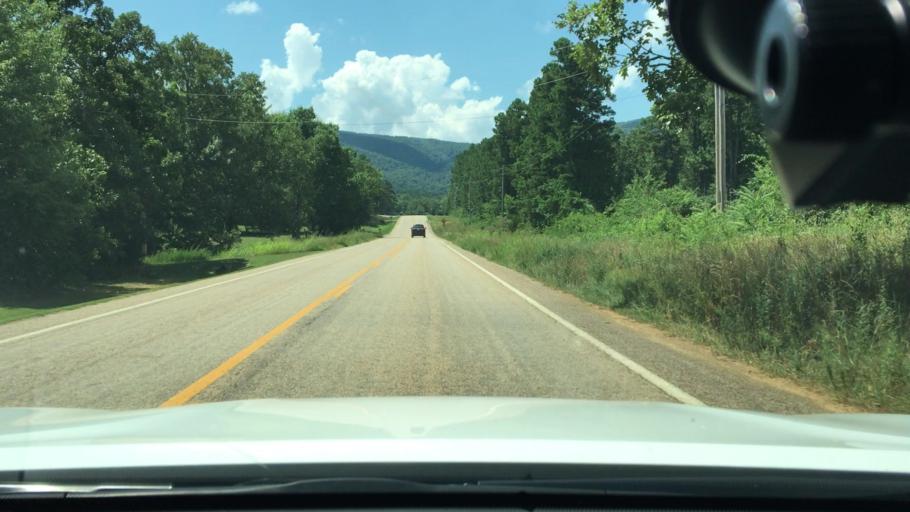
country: US
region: Arkansas
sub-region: Logan County
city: Paris
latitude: 35.2019
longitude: -93.6348
